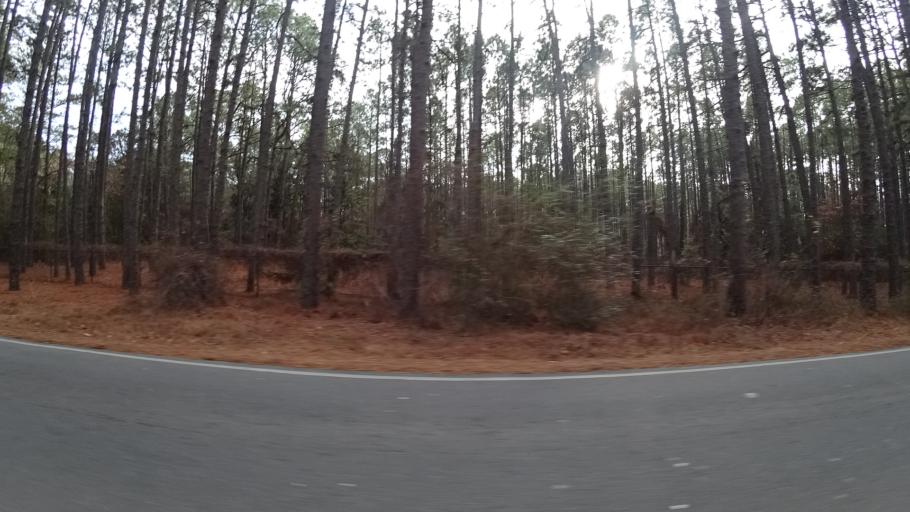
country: US
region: North Carolina
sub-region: Moore County
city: Pinehurst
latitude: 35.1770
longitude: -79.4354
